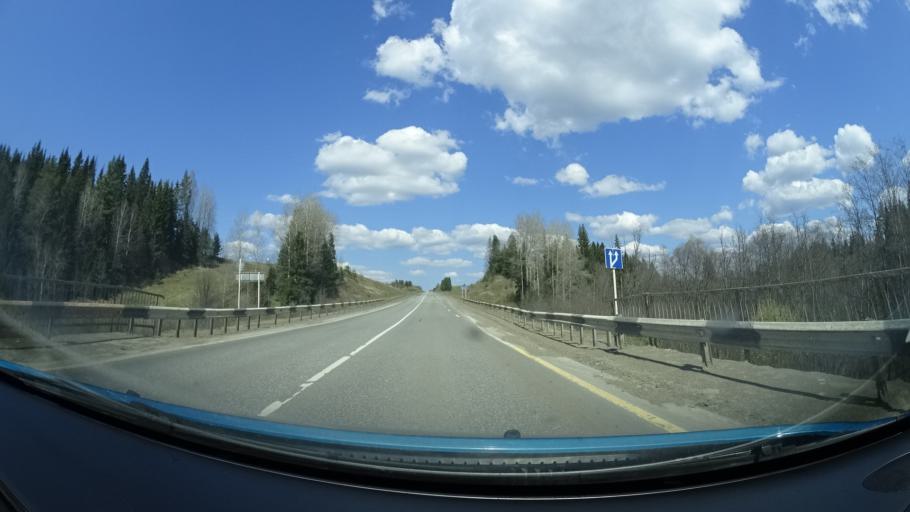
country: RU
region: Perm
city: Yugo-Kamskiy
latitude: 57.4852
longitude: 55.6818
